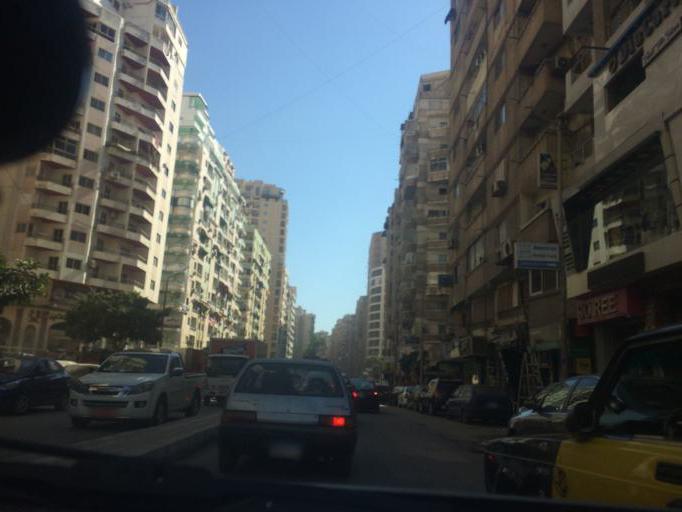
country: EG
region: Alexandria
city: Alexandria
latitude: 31.2741
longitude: 30.0056
